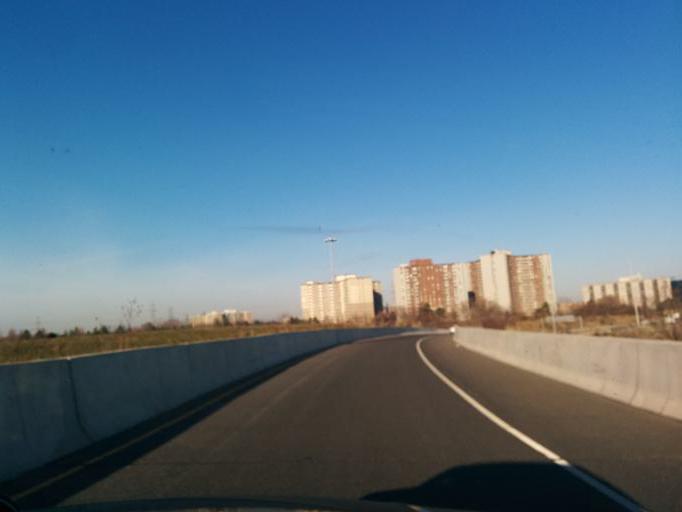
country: CA
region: Ontario
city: Etobicoke
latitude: 43.6717
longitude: -79.5725
